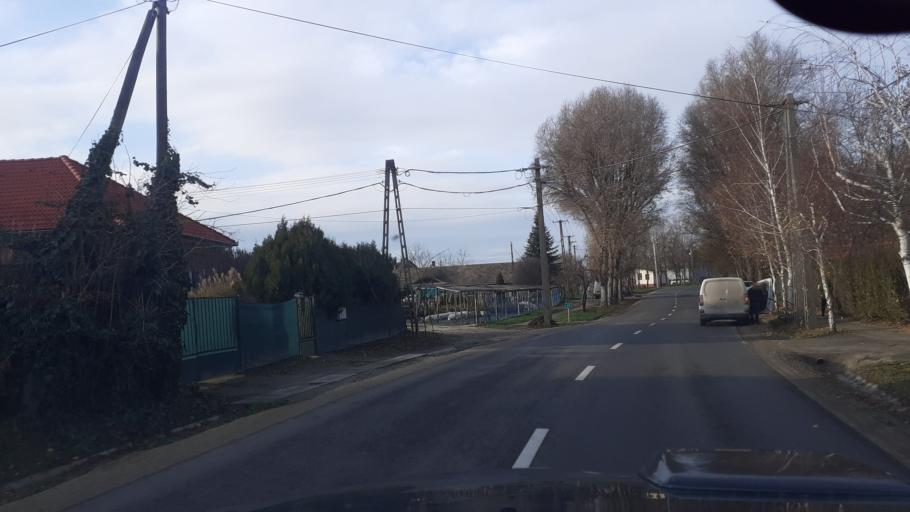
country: HU
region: Bacs-Kiskun
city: Tass
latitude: 47.0241
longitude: 19.0258
